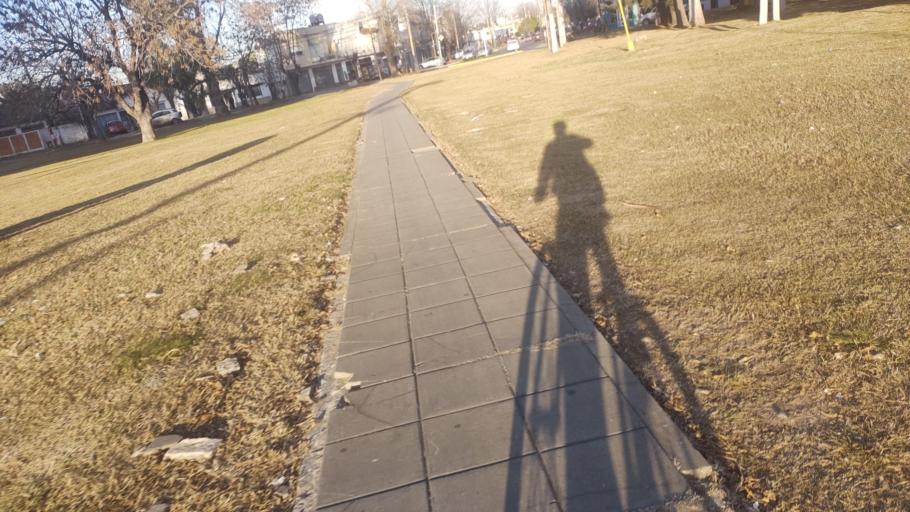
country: AR
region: Buenos Aires
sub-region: Partido de La Plata
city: La Plata
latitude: -34.9199
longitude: -57.9158
